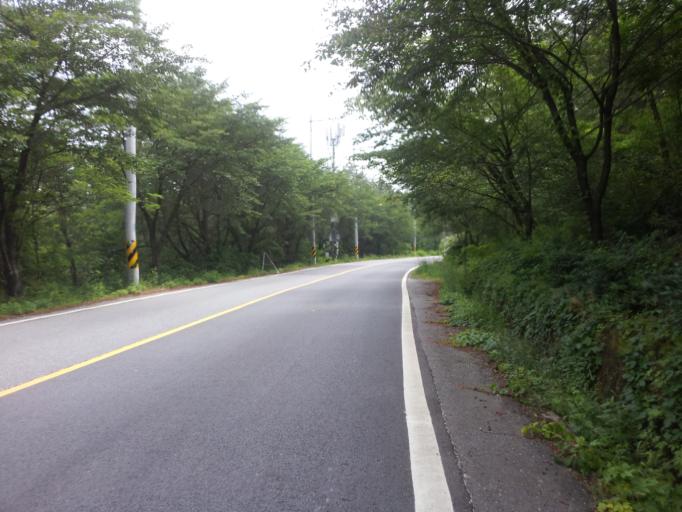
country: KR
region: Chungcheongbuk-do
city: Okcheon
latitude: 36.3908
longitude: 127.5255
